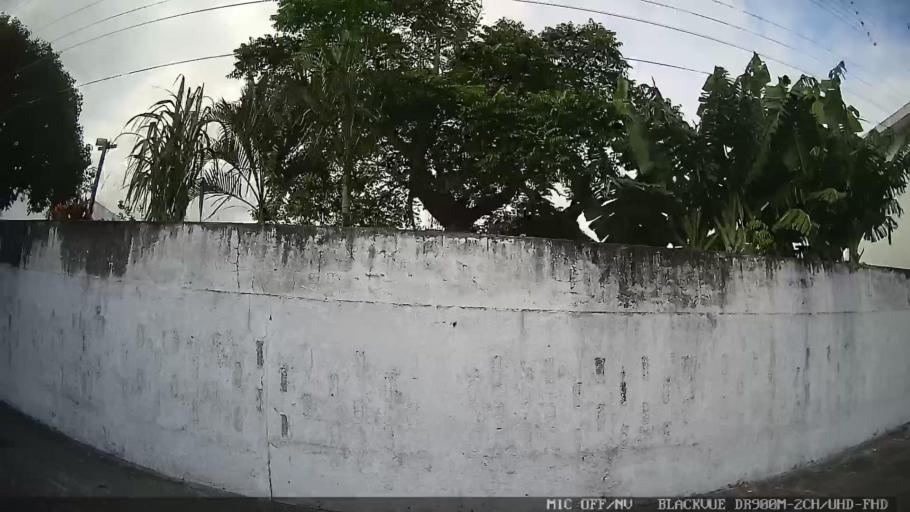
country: BR
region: Sao Paulo
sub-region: Peruibe
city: Peruibe
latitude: -24.3121
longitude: -46.9854
